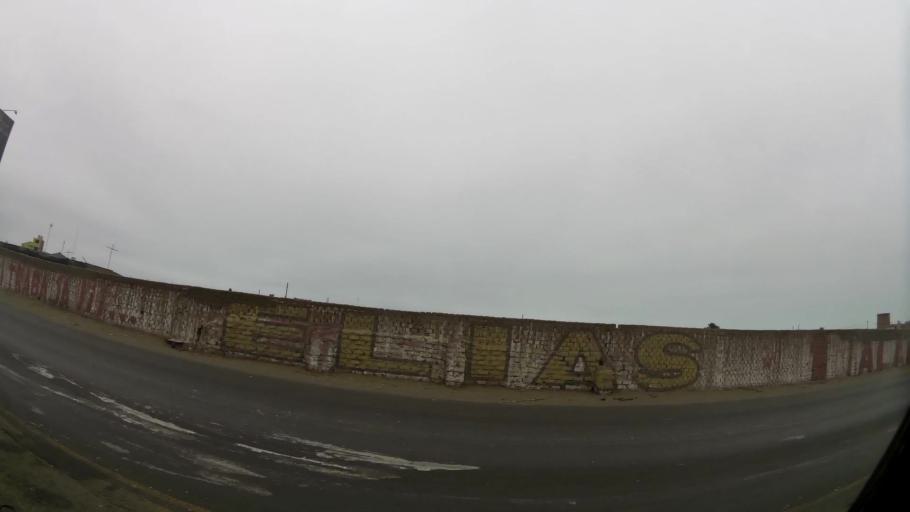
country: PE
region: La Libertad
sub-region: Provincia de Trujillo
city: Moche
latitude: -8.1667
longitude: -79.0077
